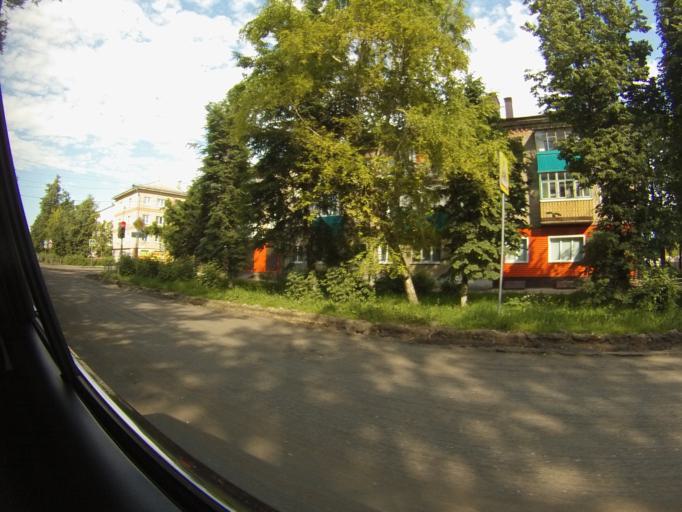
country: RU
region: Orjol
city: Mtsensk
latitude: 53.2761
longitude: 36.5771
